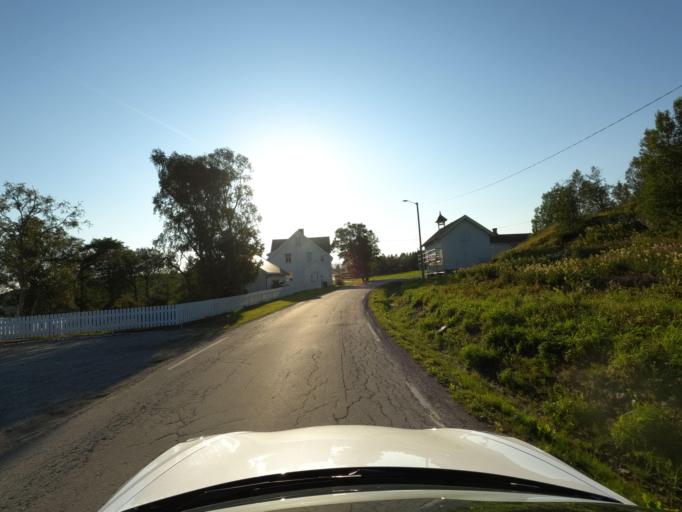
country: NO
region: Nordland
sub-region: Ballangen
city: Ballangen
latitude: 68.4584
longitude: 16.7009
